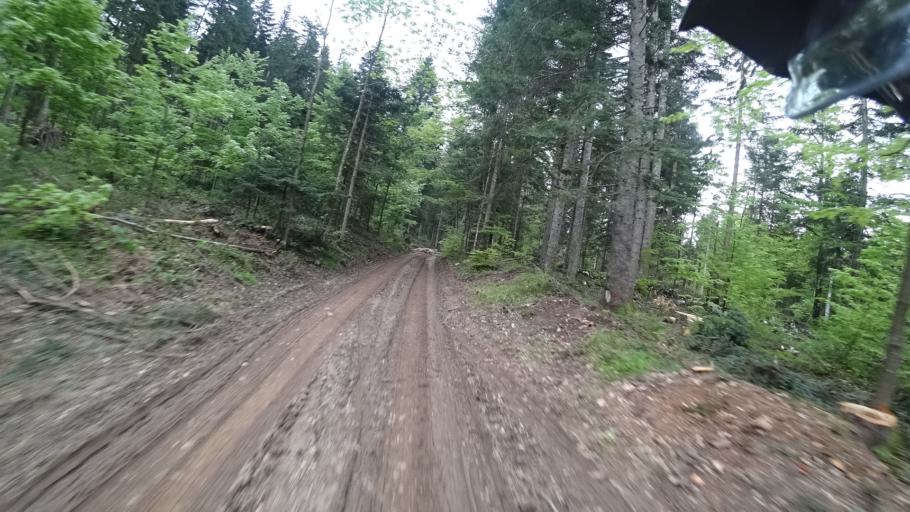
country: HR
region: Karlovacka
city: Plaski
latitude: 44.9511
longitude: 15.4151
